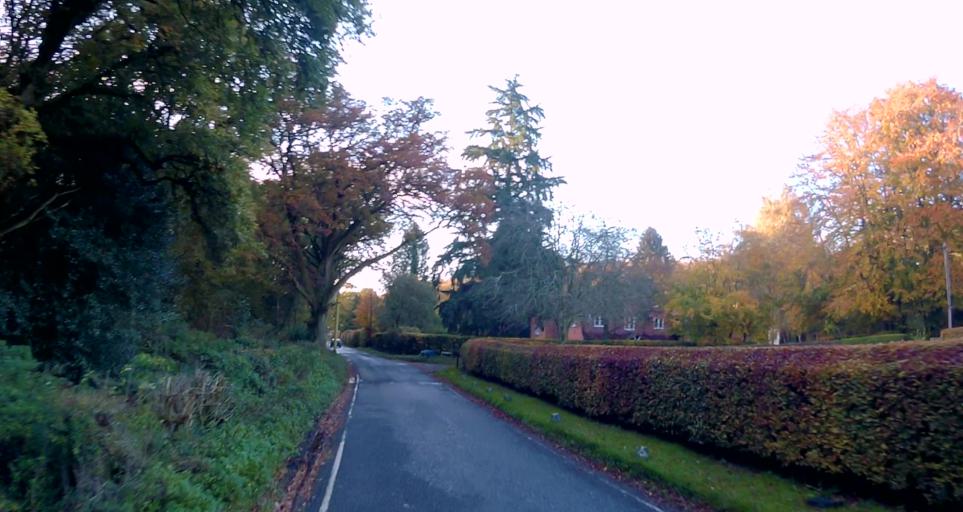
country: GB
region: England
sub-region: Hampshire
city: Basingstoke
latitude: 51.1917
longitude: -1.0916
